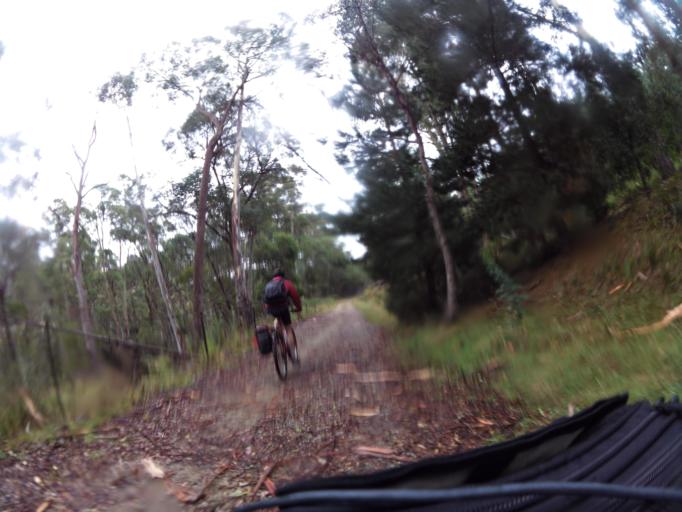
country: AU
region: New South Wales
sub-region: Greater Hume Shire
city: Holbrook
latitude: -36.1852
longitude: 147.5020
